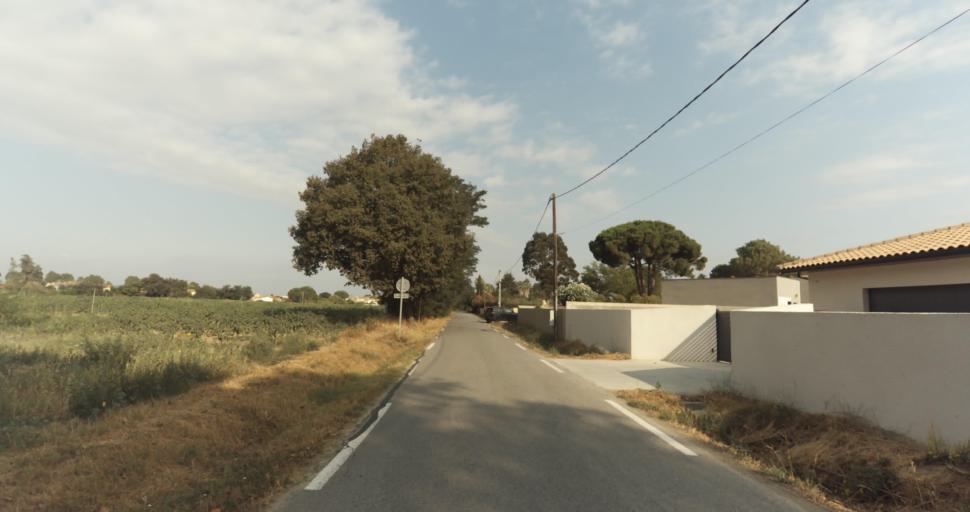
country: FR
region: Languedoc-Roussillon
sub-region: Departement des Pyrenees-Orientales
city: Corneilla-del-Vercol
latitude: 42.6224
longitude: 2.9609
